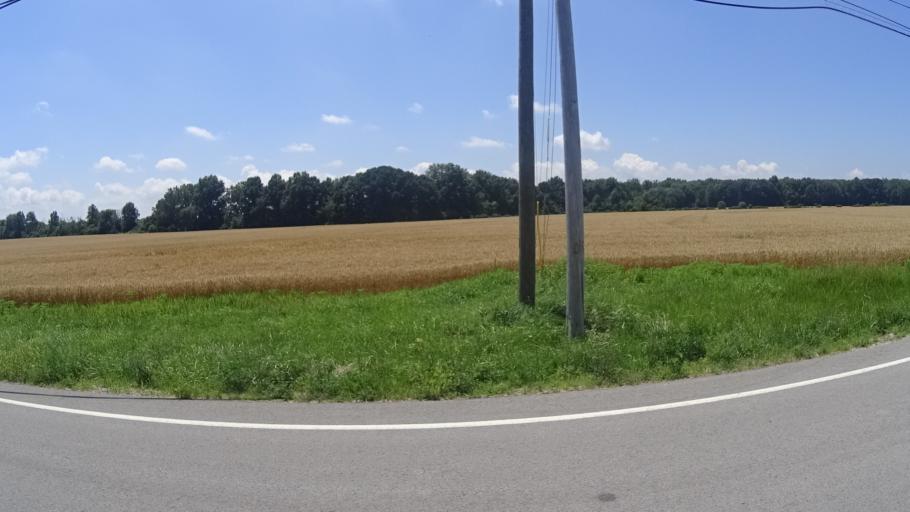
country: US
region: Ohio
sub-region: Huron County
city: Wakeman
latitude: 41.3289
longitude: -82.4143
